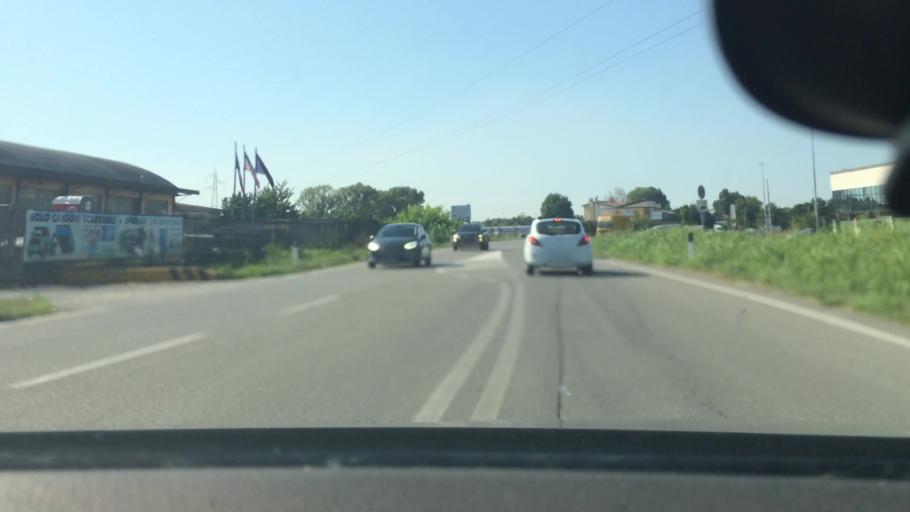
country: IT
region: Lombardy
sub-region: Provincia di Lodi
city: Guardamiglio
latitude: 45.0999
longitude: 9.6857
